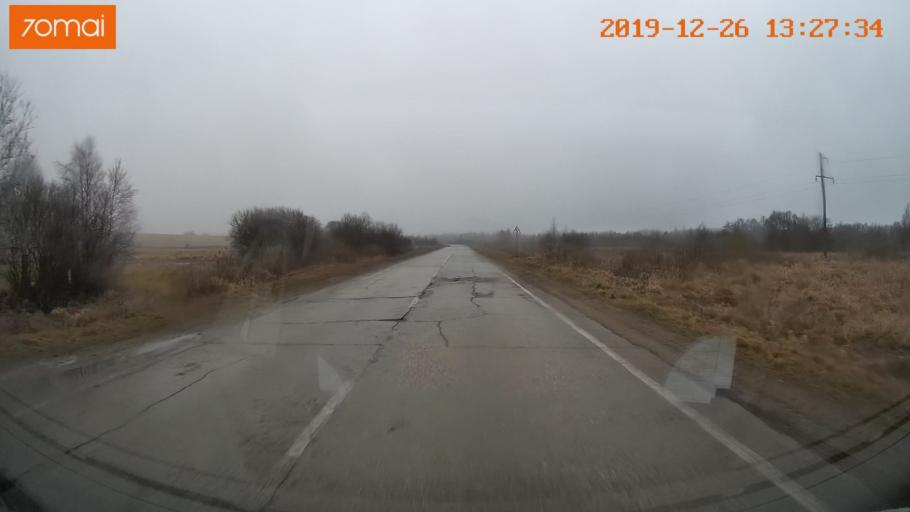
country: RU
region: Vologda
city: Cherepovets
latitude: 58.8526
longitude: 38.2414
